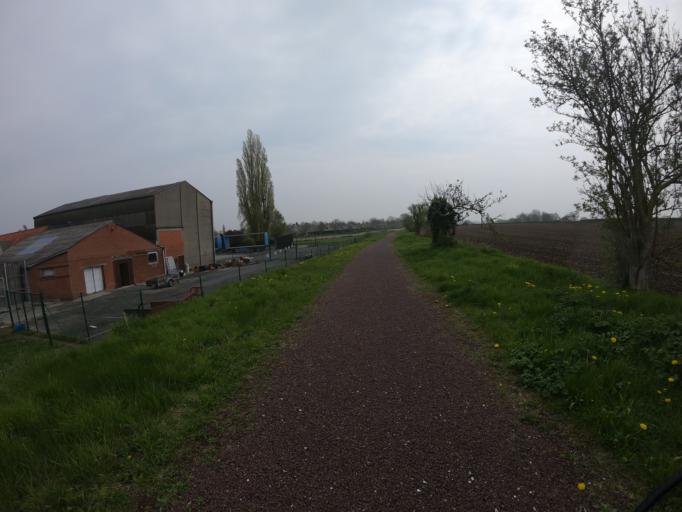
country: BE
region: Flanders
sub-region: Provincie West-Vlaanderen
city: Avelgem
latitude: 50.7793
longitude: 3.4016
